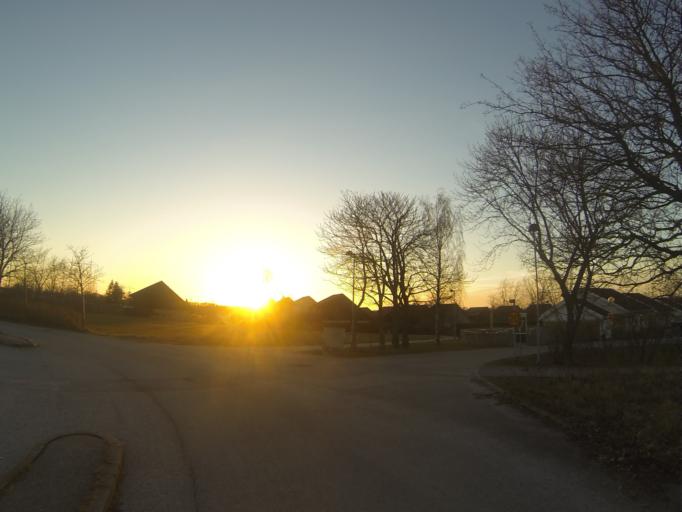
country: SE
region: Skane
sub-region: Lunds Kommun
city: Genarp
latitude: 55.7071
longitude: 13.3348
